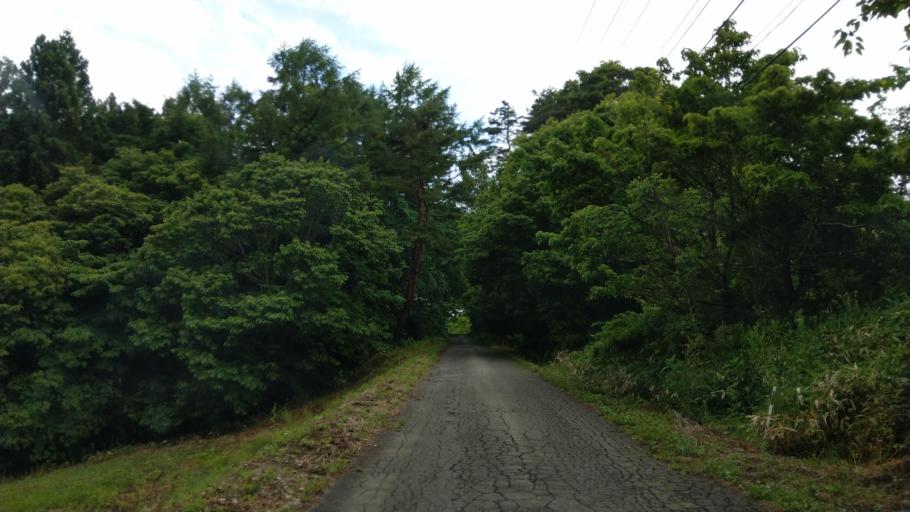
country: JP
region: Nagano
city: Komoro
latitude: 36.2840
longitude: 138.3749
